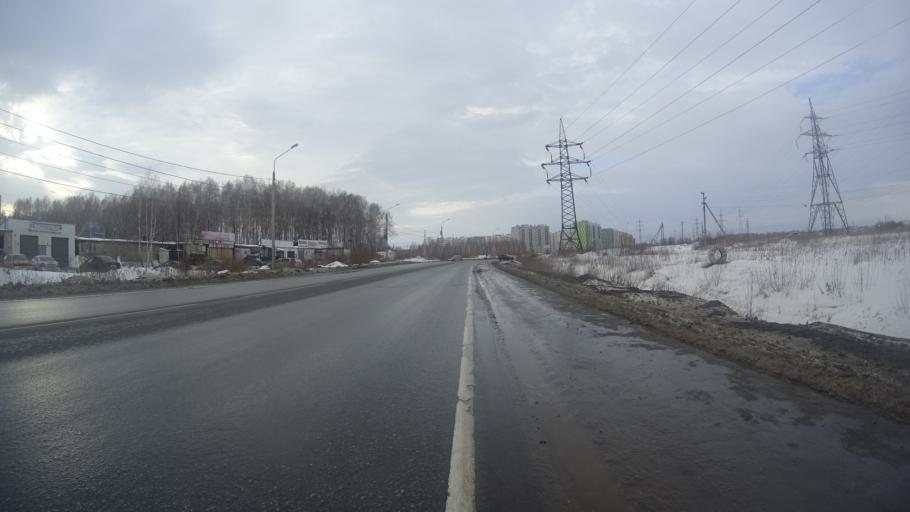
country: RU
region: Chelyabinsk
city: Roshchino
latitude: 55.2108
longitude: 61.3109
